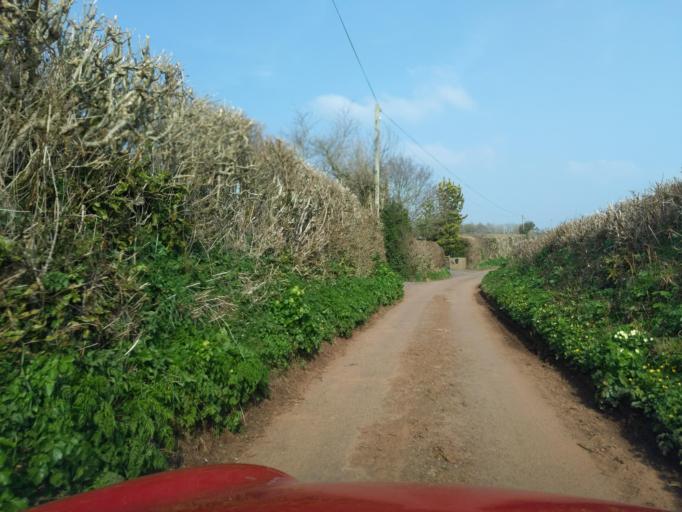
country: GB
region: England
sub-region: Devon
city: Kingsbridge
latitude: 50.2865
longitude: -3.7201
